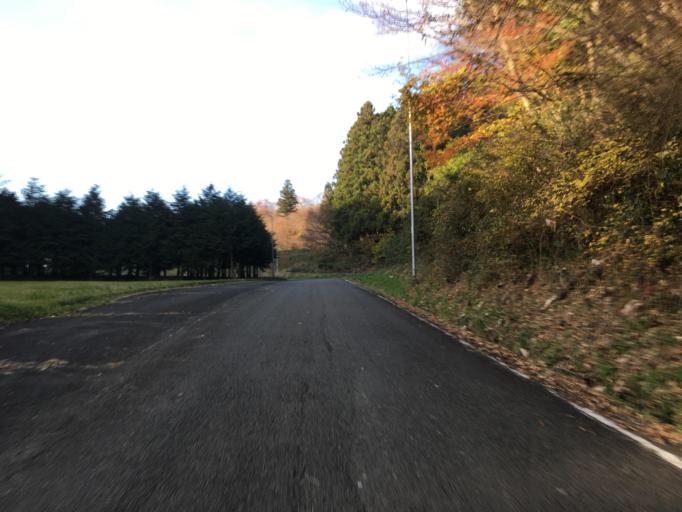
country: JP
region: Fukushima
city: Ishikawa
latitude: 37.2446
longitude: 140.5863
